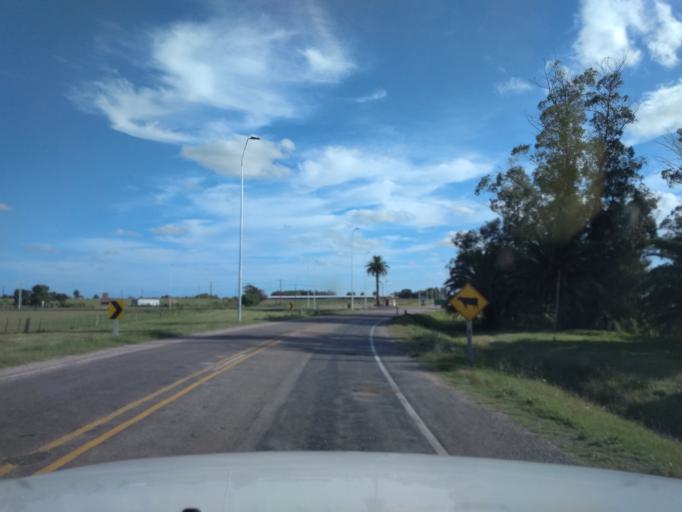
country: UY
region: Canelones
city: San Ramon
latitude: -34.2417
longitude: -55.9253
